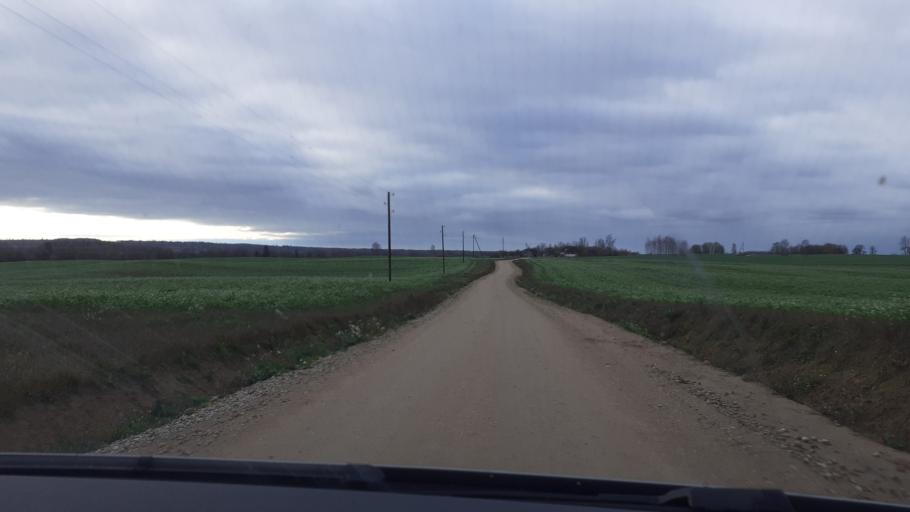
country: LV
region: Aizpute
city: Aizpute
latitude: 56.7684
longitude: 21.8053
